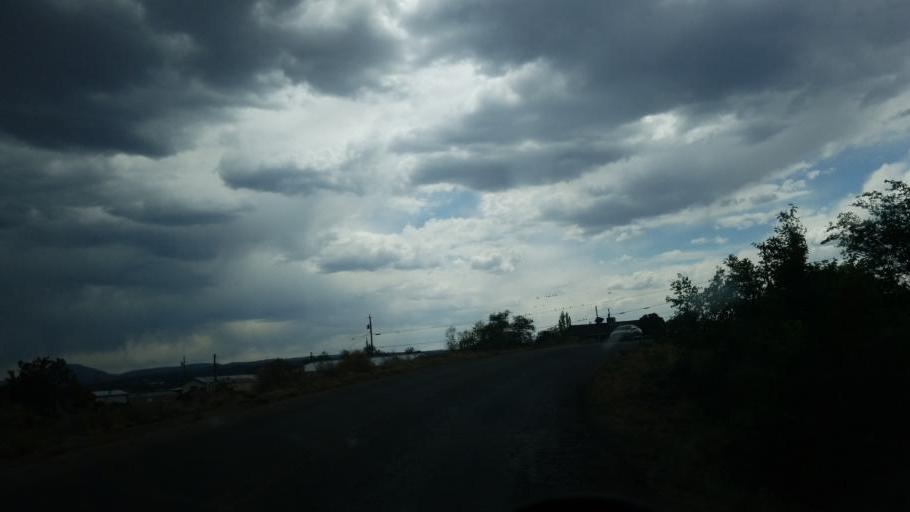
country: US
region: New Mexico
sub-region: Cibola County
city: Grants
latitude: 35.1574
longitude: -107.8529
